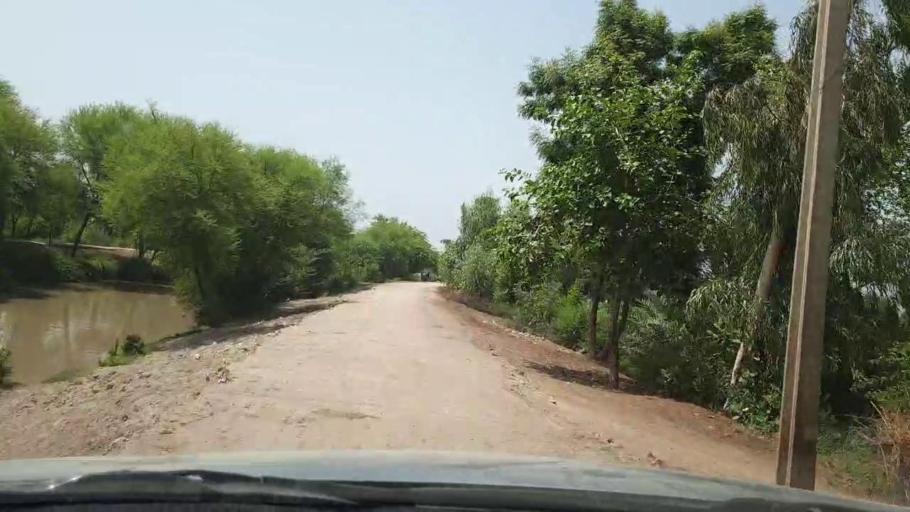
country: PK
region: Sindh
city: Pano Aqil
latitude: 27.9227
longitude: 69.1639
